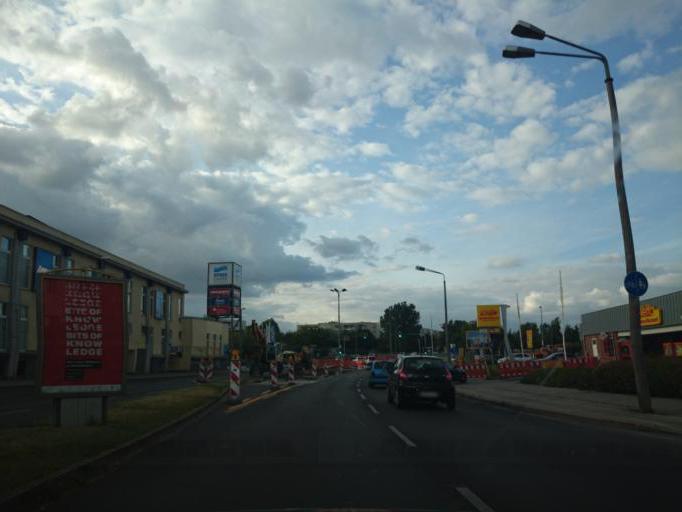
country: DE
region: Berlin
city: Kaulsdorf
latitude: 52.5224
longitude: 13.5875
